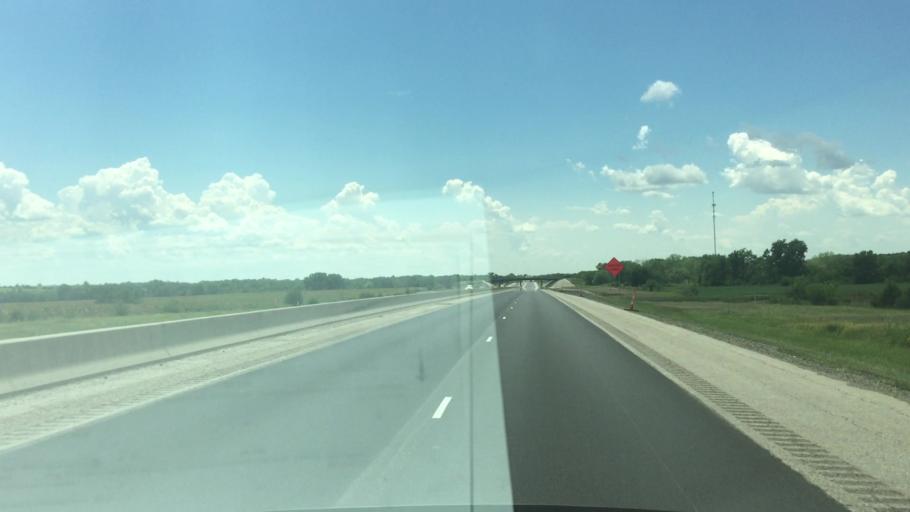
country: US
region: Kansas
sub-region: Osage County
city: Osage City
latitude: 38.7441
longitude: -95.9481
